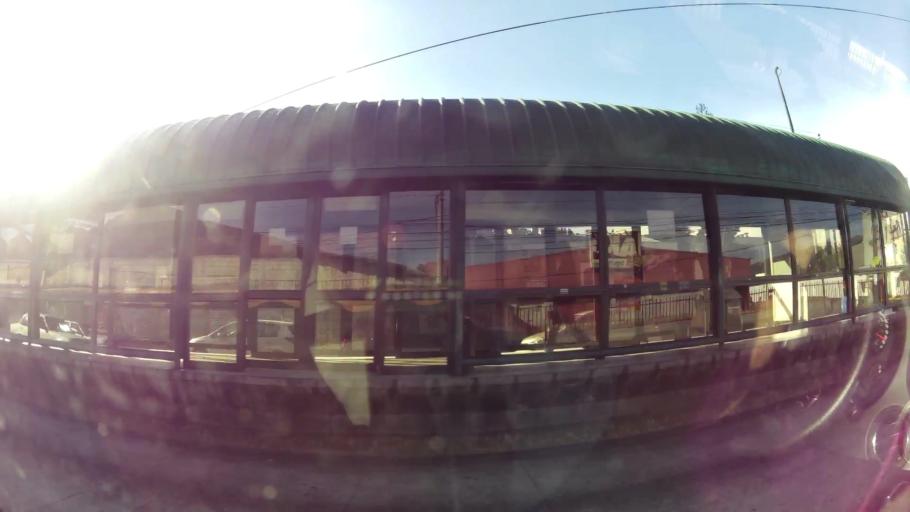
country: EC
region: Pichincha
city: Quito
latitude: -0.2829
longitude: -78.5352
